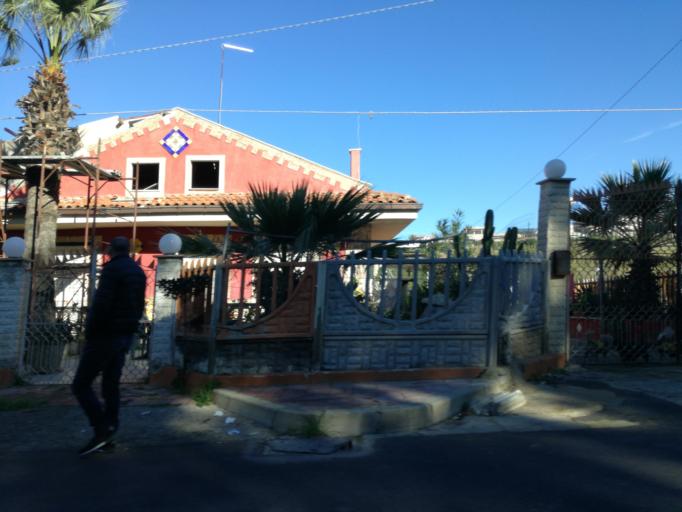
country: IT
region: Sicily
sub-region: Provincia di Caltanissetta
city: Gela
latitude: 37.0736
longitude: 14.2215
